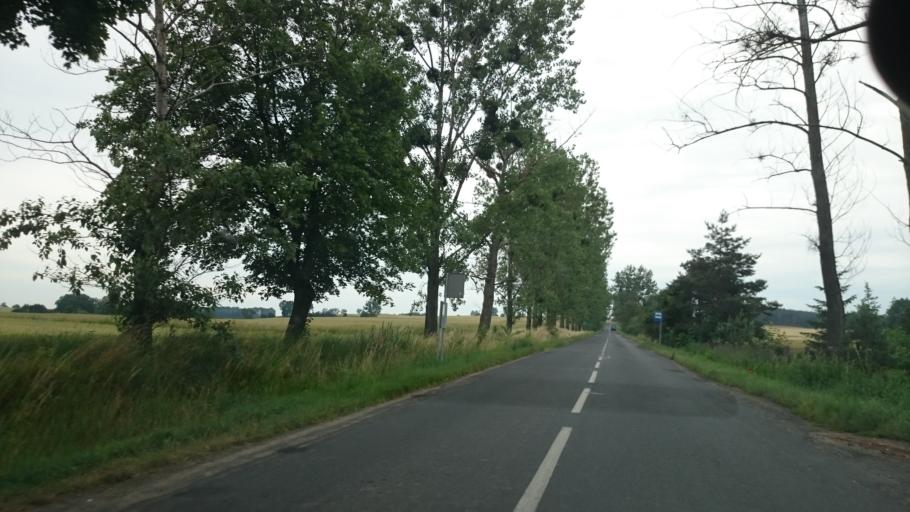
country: PL
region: Lower Silesian Voivodeship
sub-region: Powiat strzelinski
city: Przeworno
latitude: 50.6575
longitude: 17.2495
